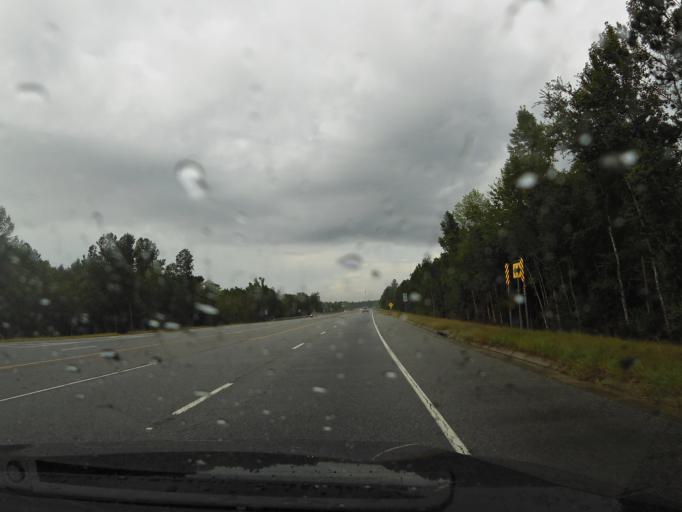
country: US
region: Georgia
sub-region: Wayne County
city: Jesup
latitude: 31.5639
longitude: -81.8367
